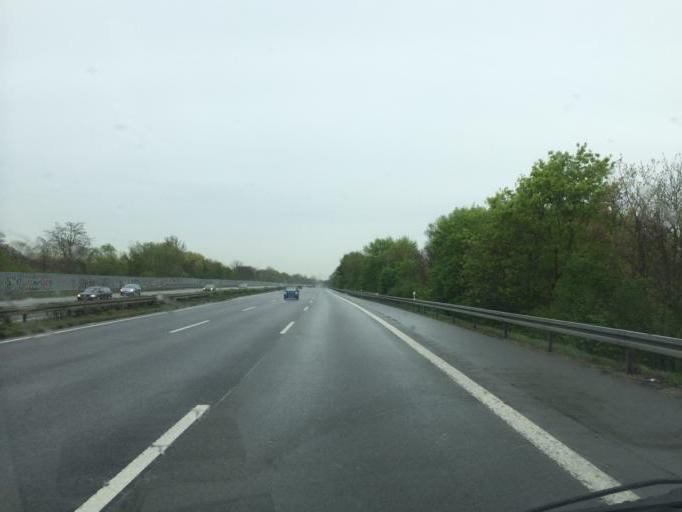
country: DE
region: North Rhine-Westphalia
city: Castrop-Rauxel
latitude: 51.6002
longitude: 7.2907
